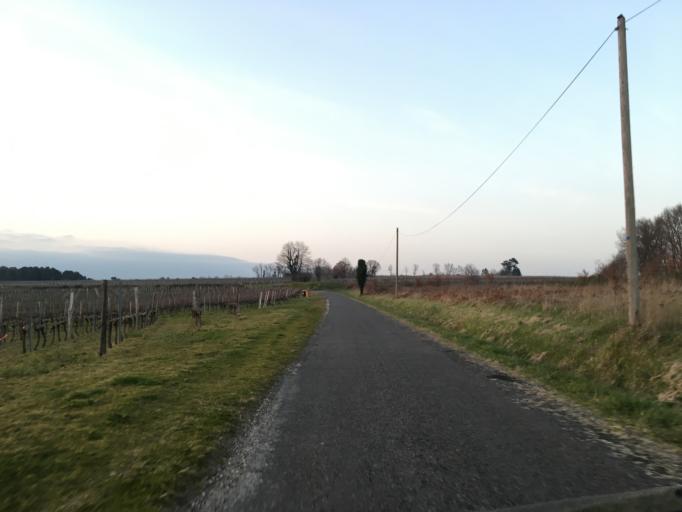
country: FR
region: Aquitaine
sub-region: Departement de la Gironde
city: Saint-Ciers-sur-Gironde
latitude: 45.3013
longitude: -0.6047
